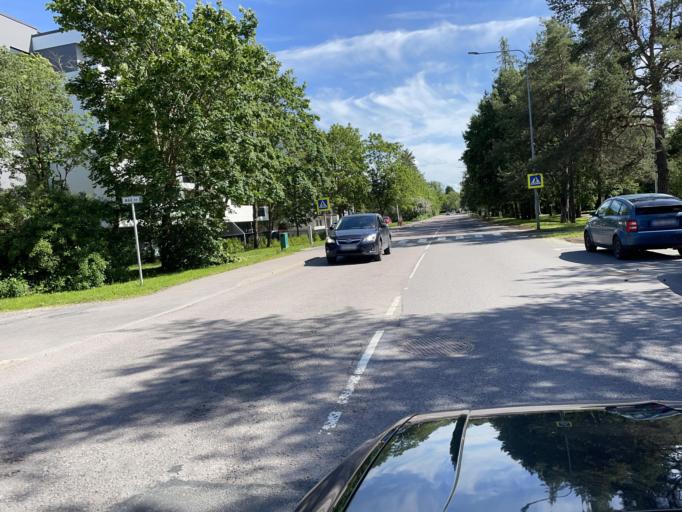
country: EE
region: Harju
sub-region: Keila linn
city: Keila
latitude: 59.3129
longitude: 24.4143
